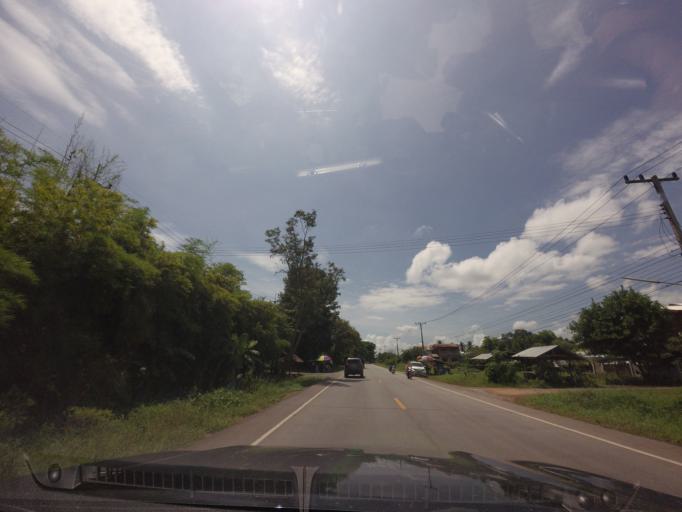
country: TH
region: Changwat Udon Thani
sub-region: Amphoe Ban Phue
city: Ban Phue
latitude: 17.7302
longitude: 102.3956
